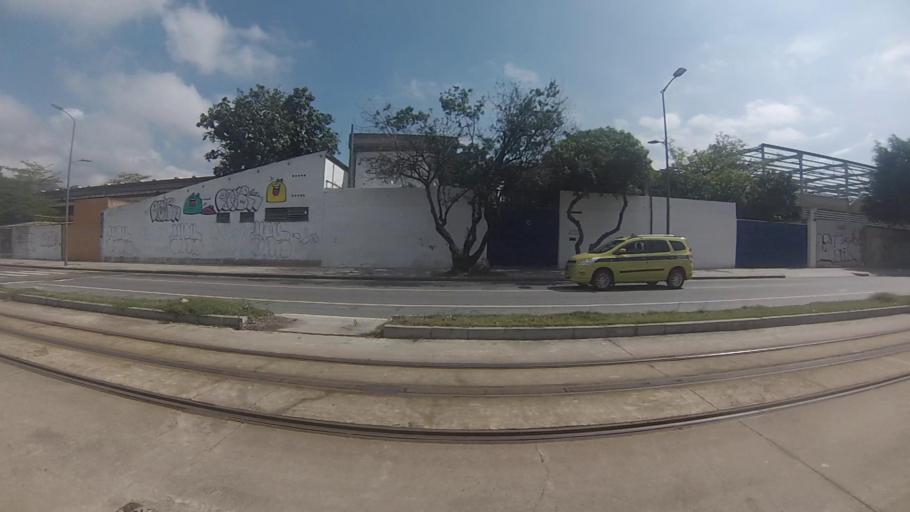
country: BR
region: Rio de Janeiro
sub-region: Rio De Janeiro
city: Rio de Janeiro
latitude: -22.9027
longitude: -43.2081
